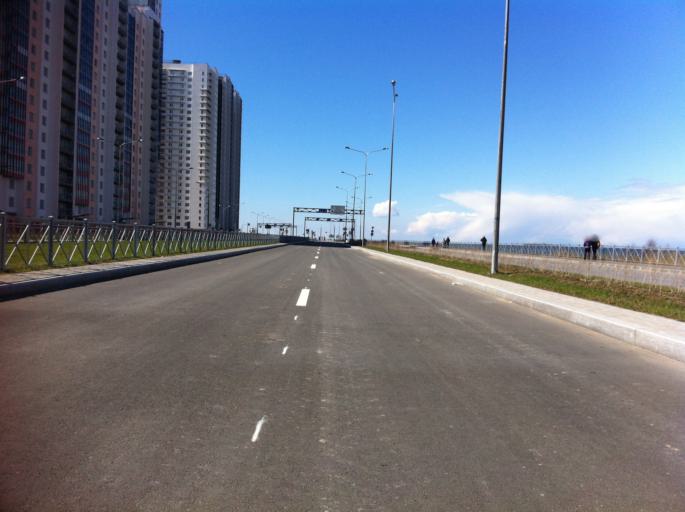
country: RU
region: St.-Petersburg
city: Uritsk
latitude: 59.8697
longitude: 30.1644
